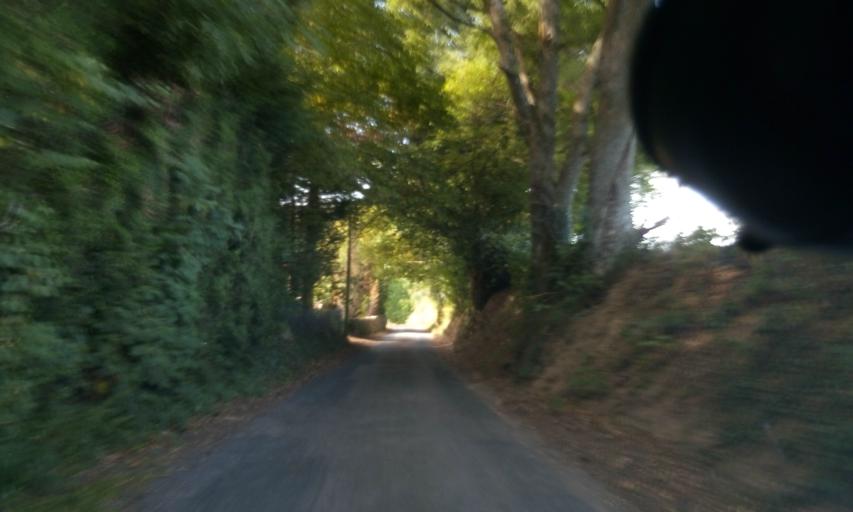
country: FR
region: Rhone-Alpes
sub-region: Departement du Rhone
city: Cublize
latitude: 45.9860
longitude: 4.3933
